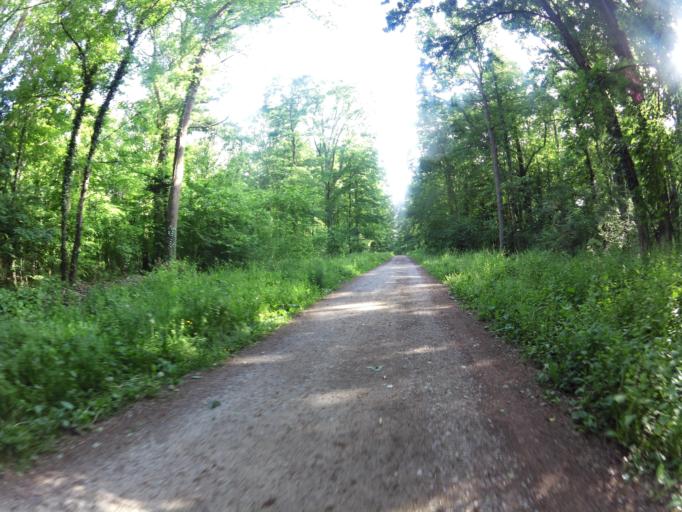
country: DE
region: Bavaria
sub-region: Regierungsbezirk Unterfranken
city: Ochsenfurt
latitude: 49.6818
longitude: 10.0687
